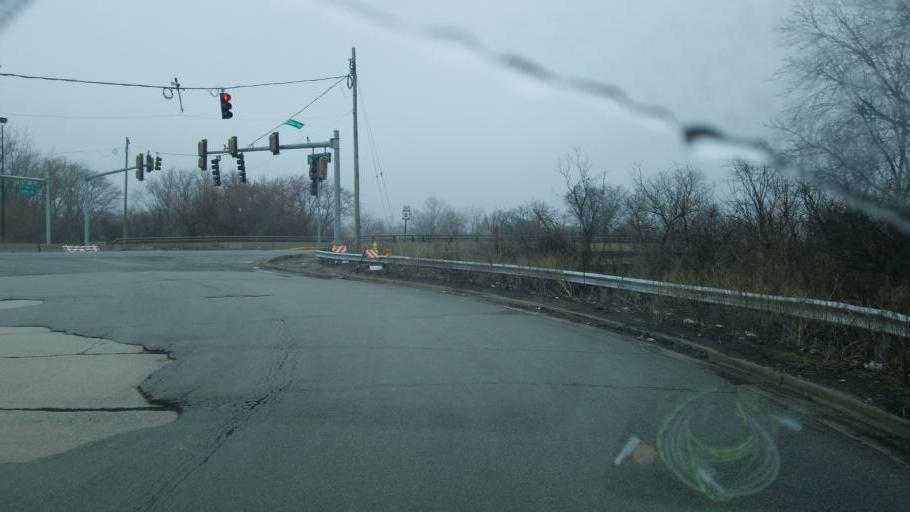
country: US
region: Illinois
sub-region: Cook County
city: South Holland
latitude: 41.6005
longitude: -87.5784
